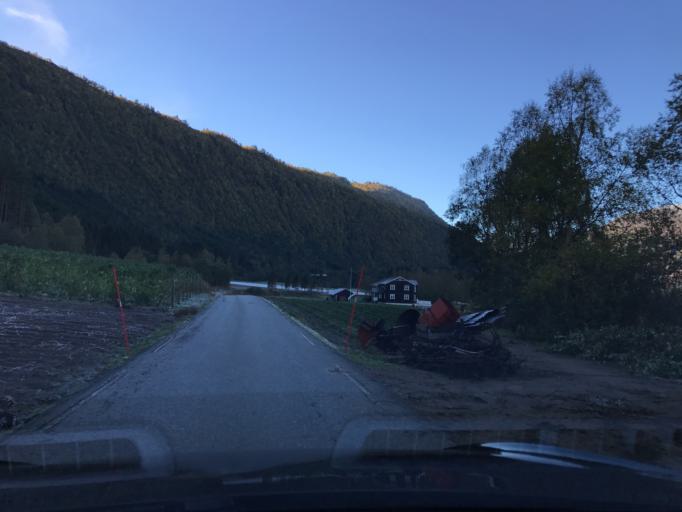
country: NO
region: More og Romsdal
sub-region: Norddal
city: Valldal
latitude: 62.3204
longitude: 7.3250
